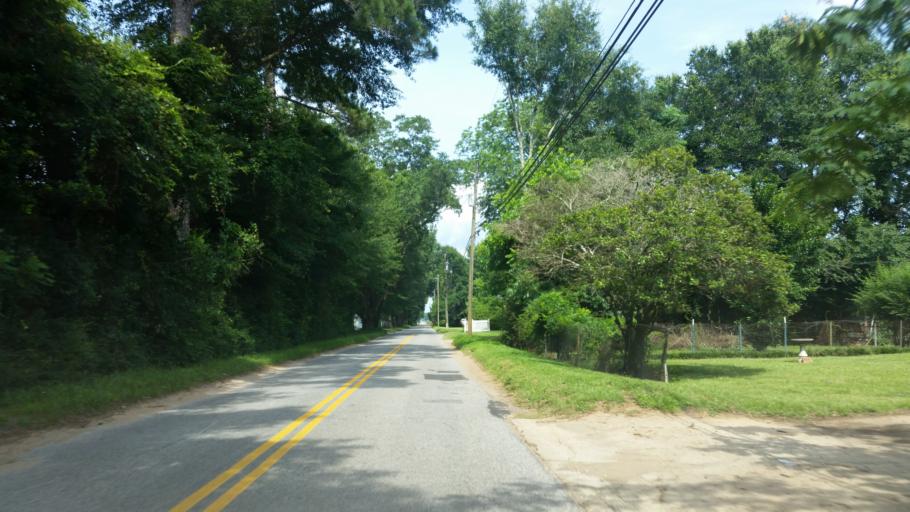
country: US
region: Florida
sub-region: Escambia County
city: Cantonment
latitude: 30.5786
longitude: -87.3564
